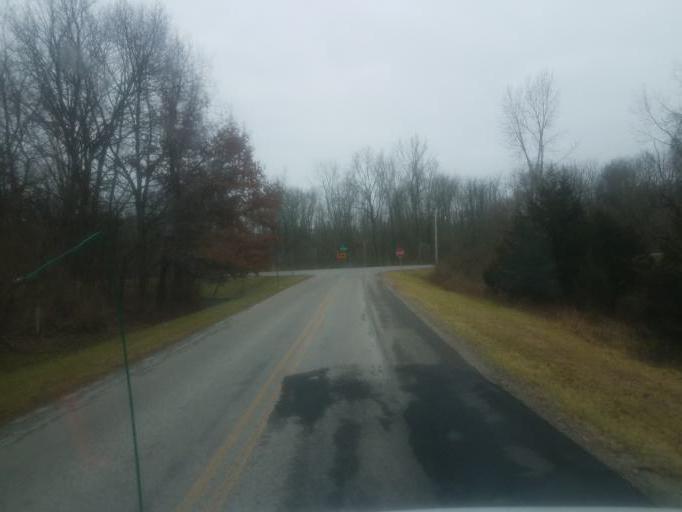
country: US
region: Ohio
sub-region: Delaware County
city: Sunbury
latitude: 40.2373
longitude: -82.8925
